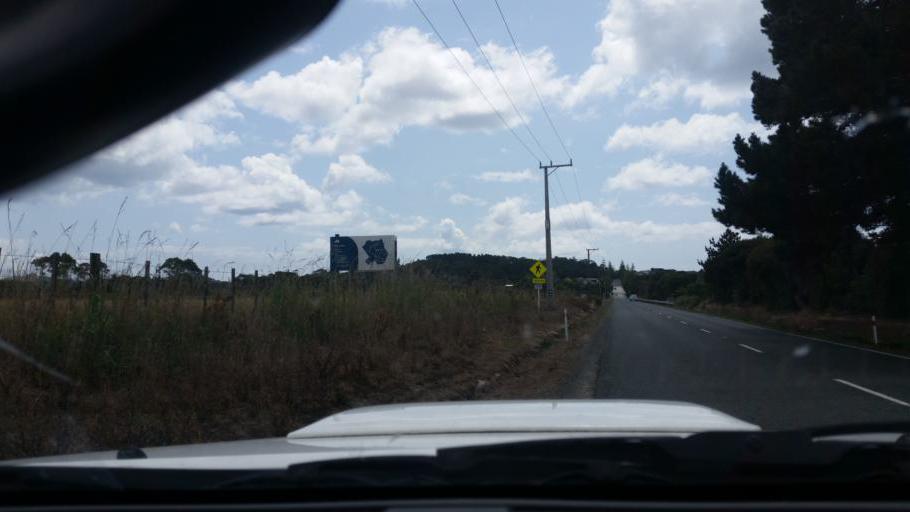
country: NZ
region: Auckland
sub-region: Auckland
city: Wellsford
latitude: -36.1111
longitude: 174.5762
